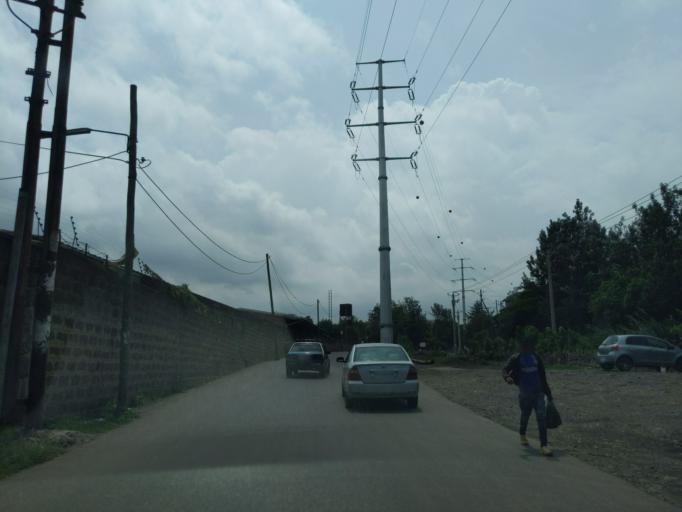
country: ET
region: Adis Abeba
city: Addis Ababa
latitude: 8.9559
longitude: 38.7607
